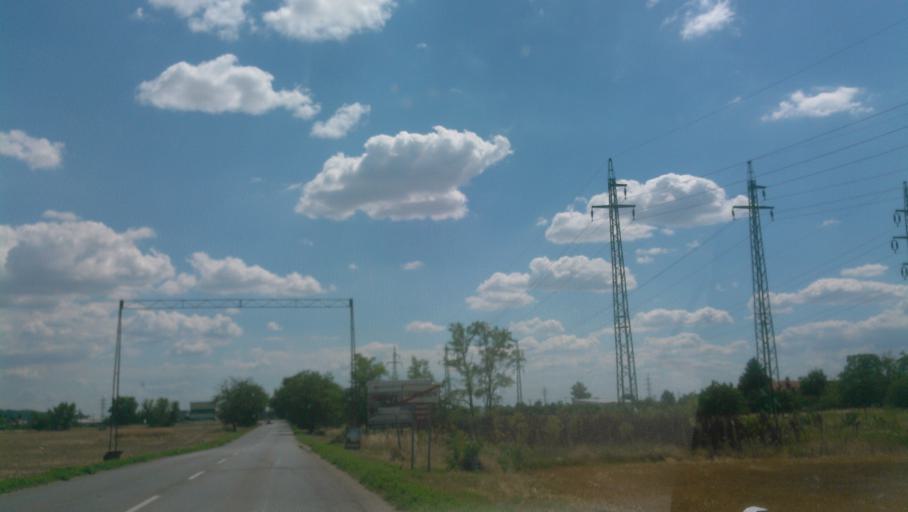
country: SK
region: Trnavsky
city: Leopoldov
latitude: 48.4395
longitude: 17.7677
